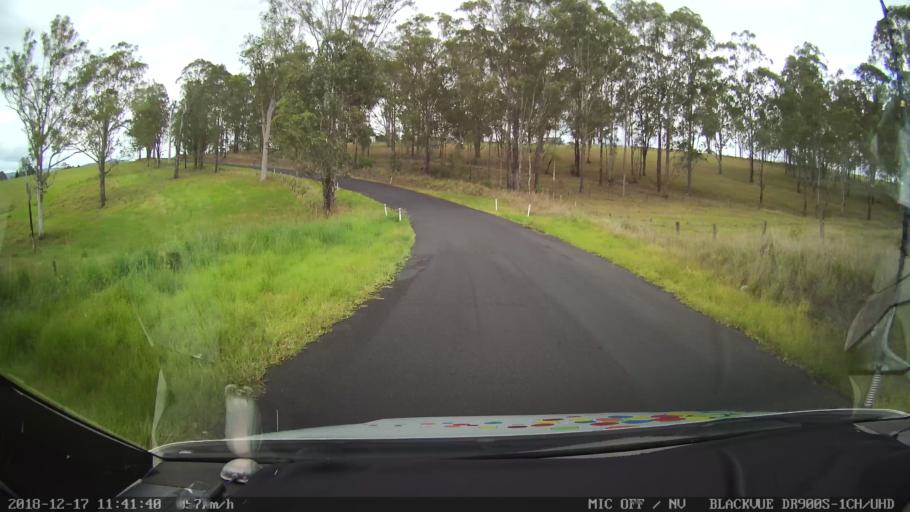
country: AU
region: New South Wales
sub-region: Kyogle
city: Kyogle
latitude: -28.6728
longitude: 152.5883
